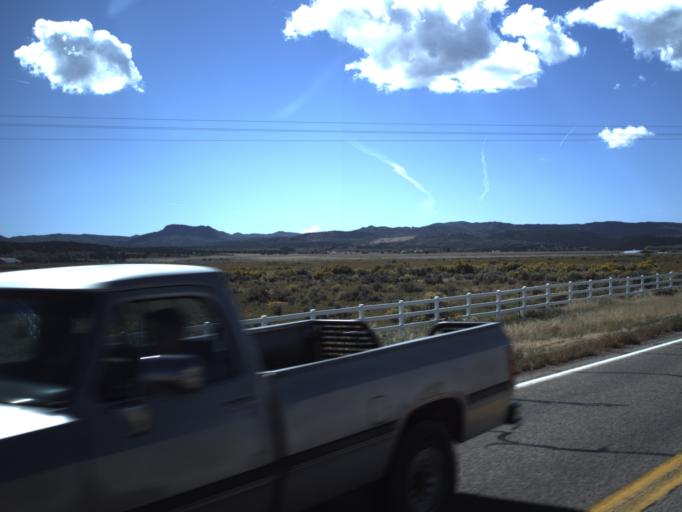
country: US
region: Utah
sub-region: Washington County
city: Enterprise
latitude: 37.5751
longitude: -113.7001
